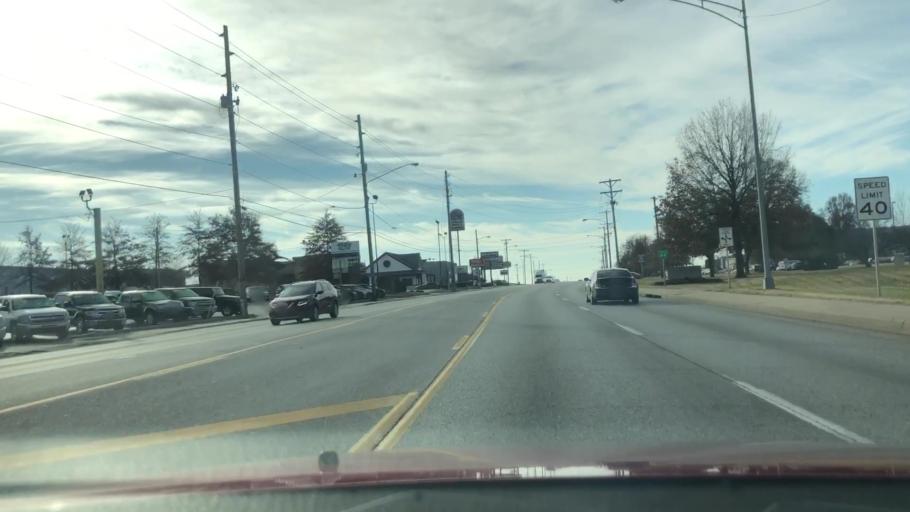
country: US
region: Missouri
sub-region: Greene County
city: Springfield
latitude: 37.2248
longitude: -93.2615
